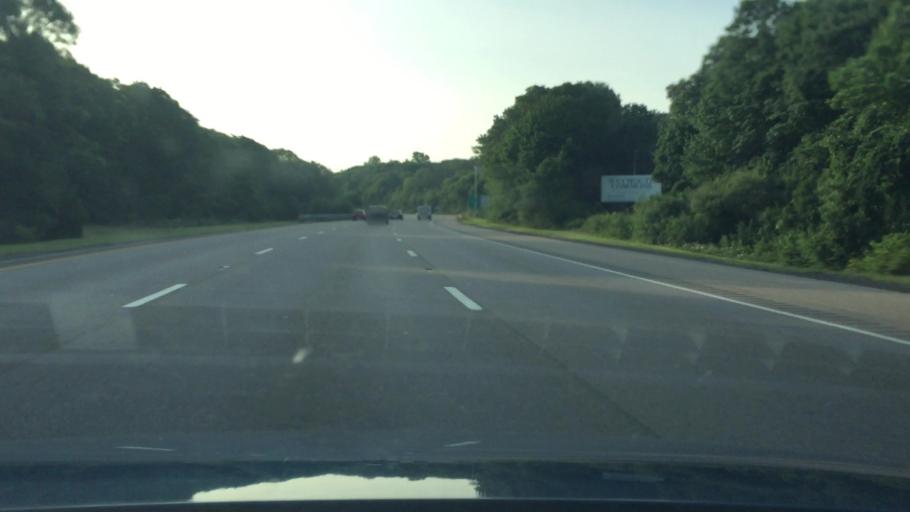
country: US
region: Massachusetts
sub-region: Norfolk County
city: Weymouth
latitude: 42.1919
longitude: -70.9481
